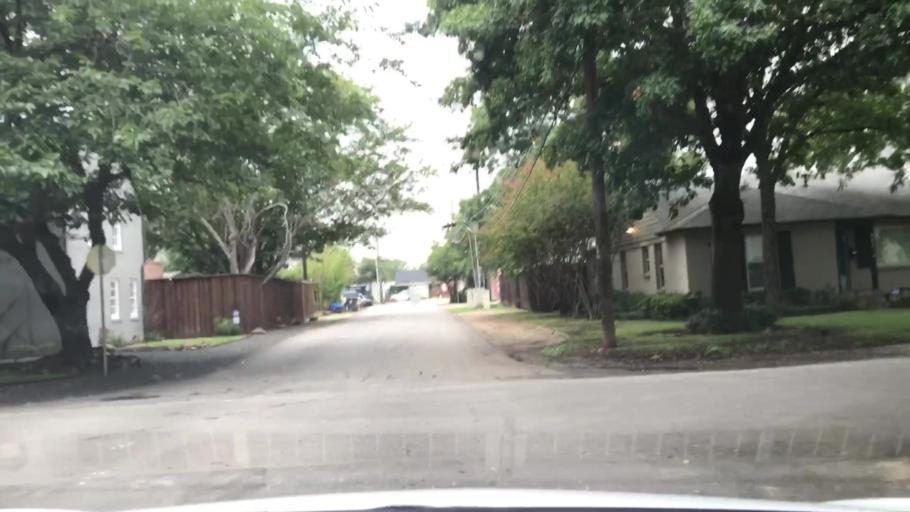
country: US
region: Texas
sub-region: Dallas County
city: University Park
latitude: 32.8524
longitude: -96.8297
